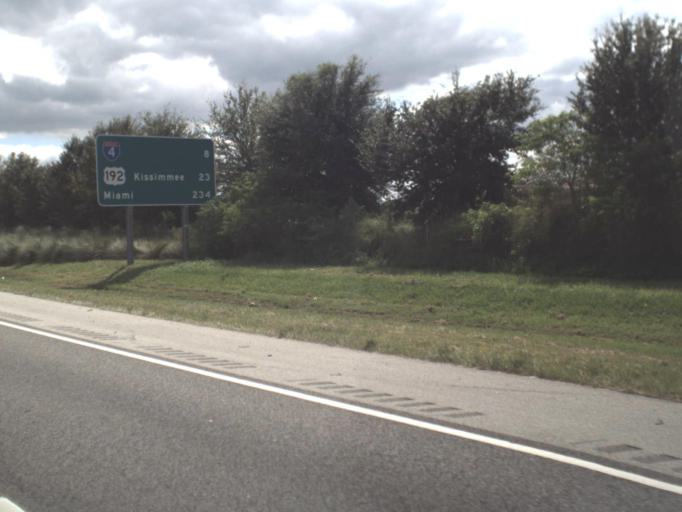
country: US
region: Florida
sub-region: Orange County
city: Gotha
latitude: 28.5434
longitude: -81.5378
